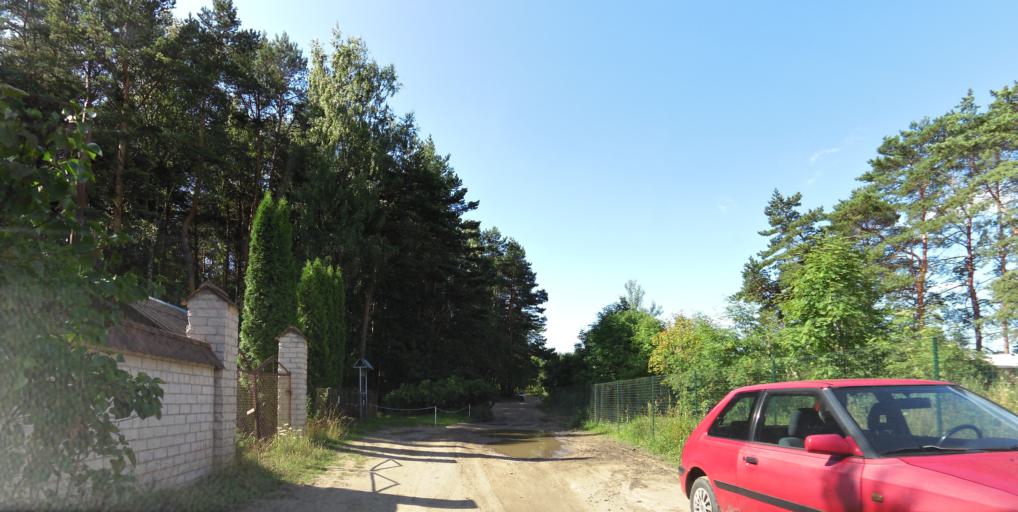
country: LT
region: Vilnius County
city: Pilaite
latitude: 54.6956
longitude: 25.1810
